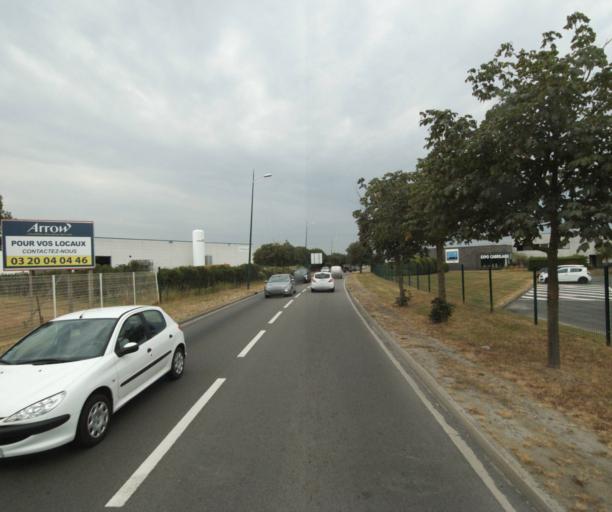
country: FR
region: Nord-Pas-de-Calais
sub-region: Departement du Nord
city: Marquette-lez-Lille
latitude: 50.6875
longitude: 3.0642
